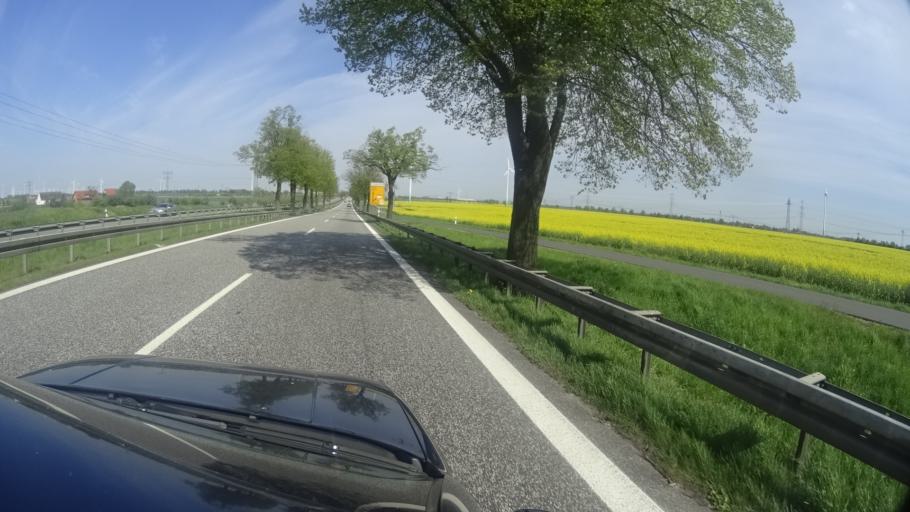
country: DE
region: Brandenburg
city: Wustermark
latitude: 52.5720
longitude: 12.9139
